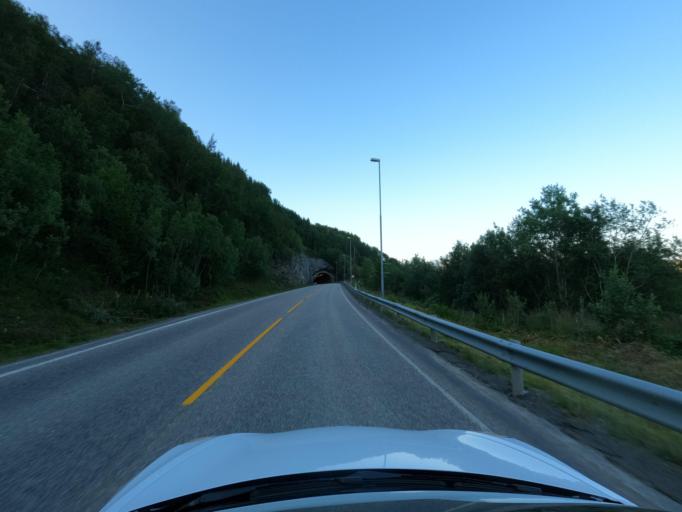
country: NO
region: Troms
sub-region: Harstad
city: Harstad
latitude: 68.7297
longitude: 16.5448
